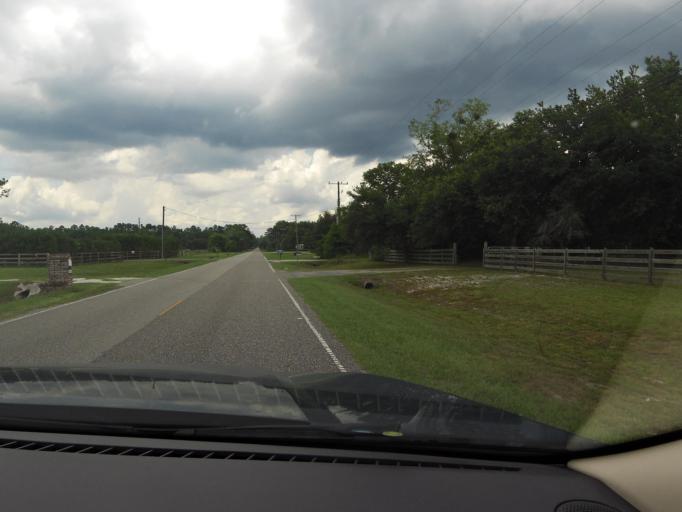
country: US
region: Florida
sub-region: Duval County
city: Baldwin
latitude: 30.3329
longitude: -81.8695
